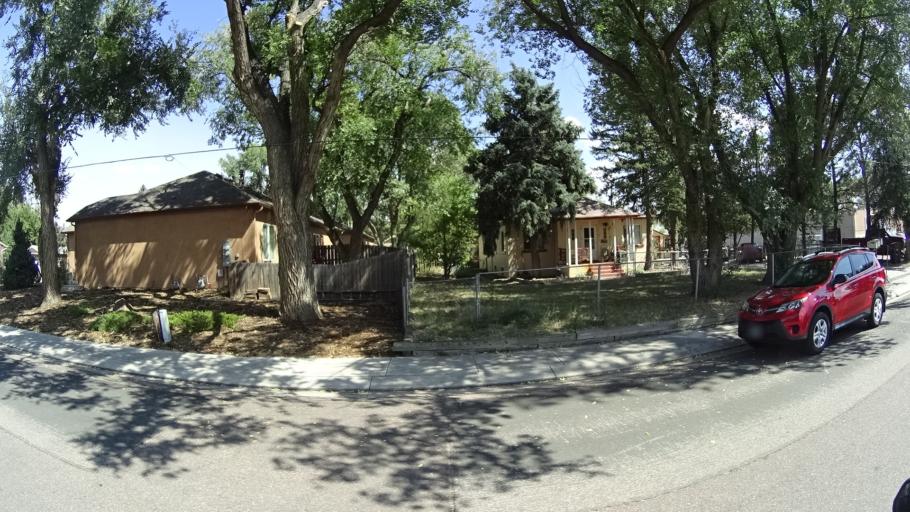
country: US
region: Colorado
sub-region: El Paso County
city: Colorado Springs
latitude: 38.8754
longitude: -104.8077
